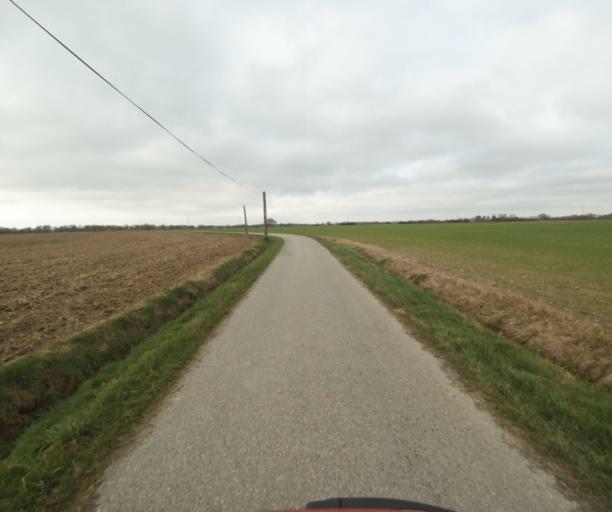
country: FR
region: Languedoc-Roussillon
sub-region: Departement de l'Aude
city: Belpech
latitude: 43.1800
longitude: 1.7155
